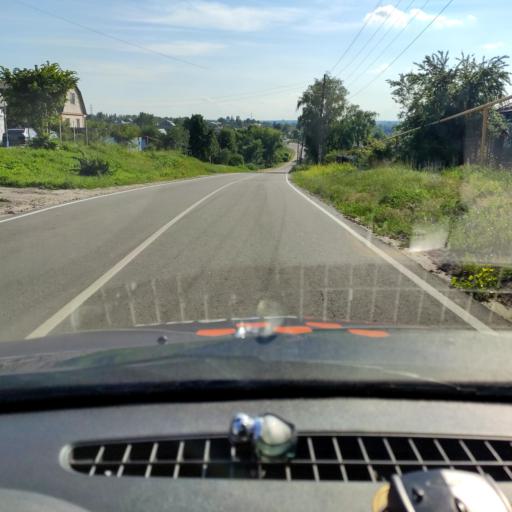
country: RU
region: Voronezj
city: Devitsa
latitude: 51.6466
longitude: 38.9664
